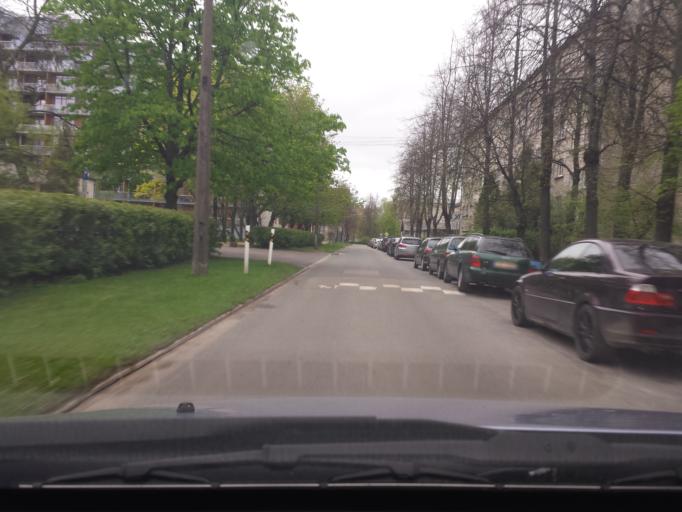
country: LV
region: Riga
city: Riga
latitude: 56.9682
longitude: 24.1293
